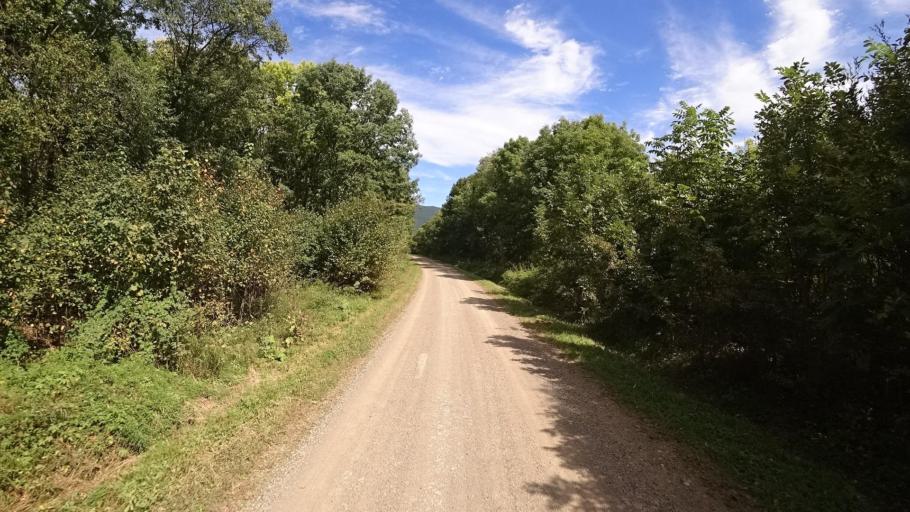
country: RU
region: Primorskiy
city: Yakovlevka
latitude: 44.6590
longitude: 133.7473
